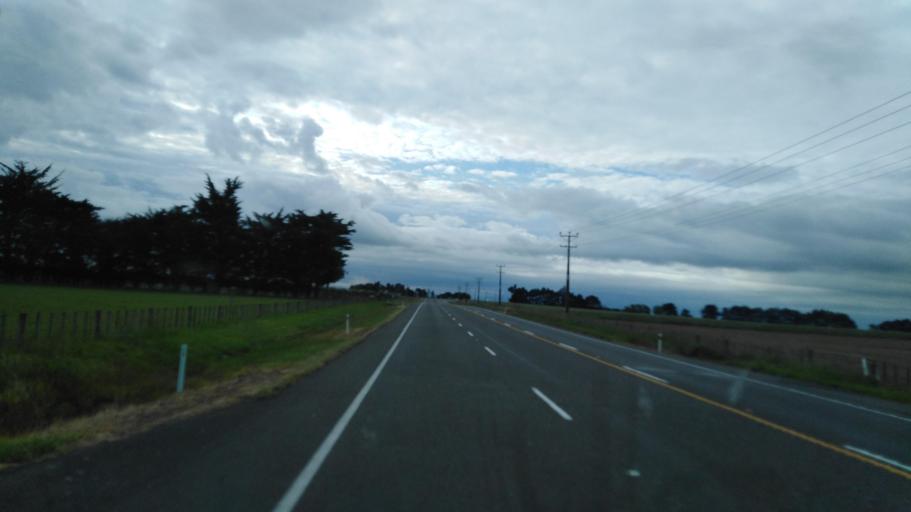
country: NZ
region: Manawatu-Wanganui
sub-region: Rangitikei District
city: Bulls
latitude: -40.1305
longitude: 175.3593
